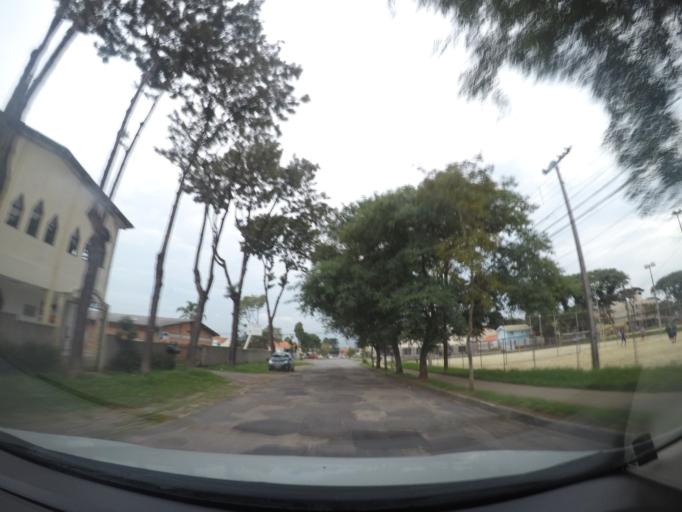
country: BR
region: Parana
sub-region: Sao Jose Dos Pinhais
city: Sao Jose dos Pinhais
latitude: -25.5172
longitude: -49.2353
